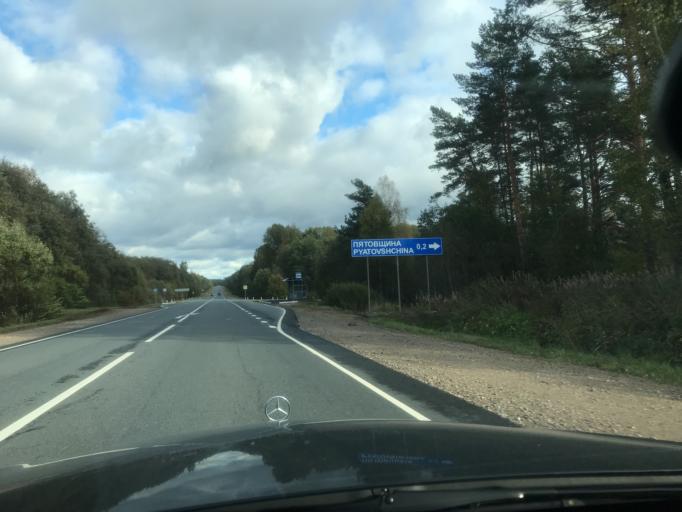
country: RU
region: Pskov
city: Pustoshka
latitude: 56.3340
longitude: 29.5491
